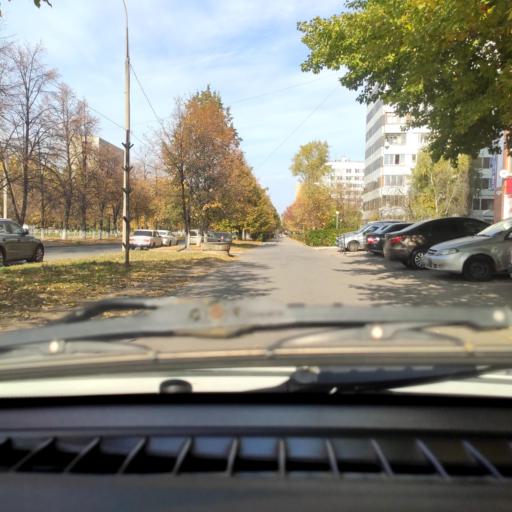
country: RU
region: Samara
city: Tol'yatti
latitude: 53.5212
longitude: 49.3112
